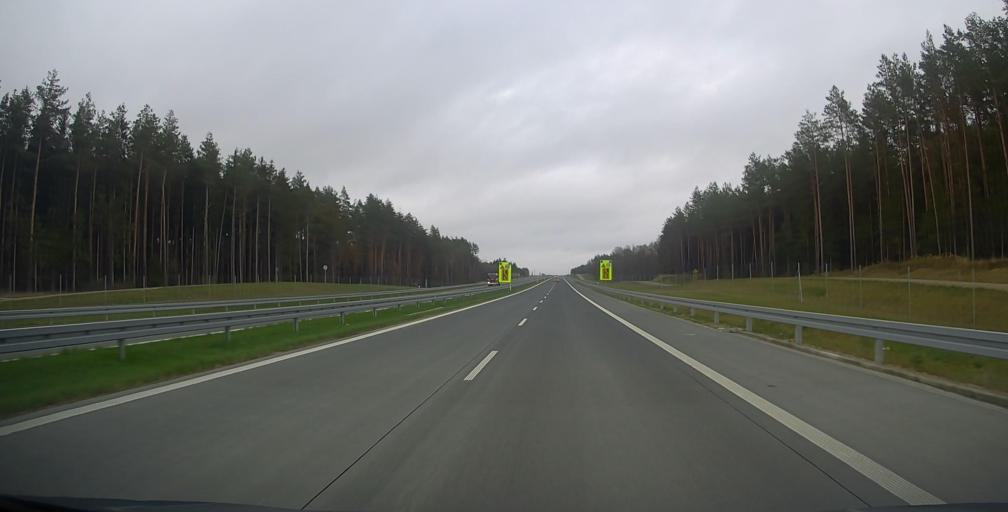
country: PL
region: Podlasie
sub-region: Powiat grajewski
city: Rajgrod
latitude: 53.8682
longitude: 22.6275
